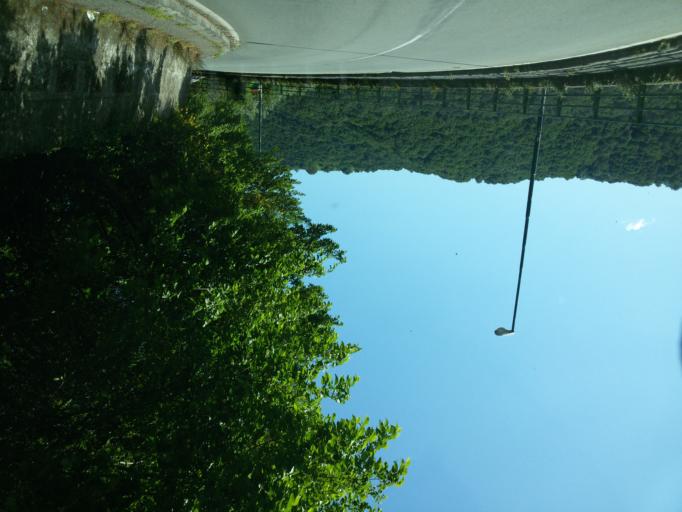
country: IT
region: Liguria
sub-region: Provincia di Genova
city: Piccarello
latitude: 44.4393
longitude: 8.9733
